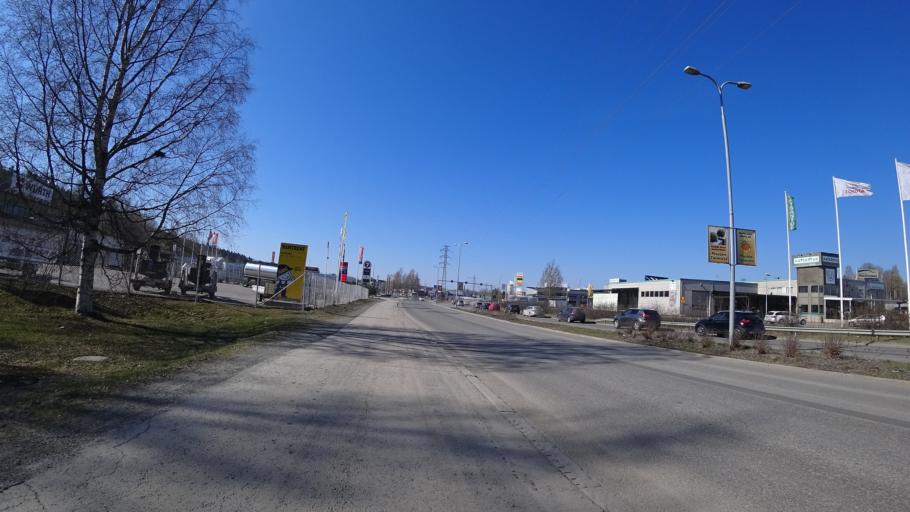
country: FI
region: Pirkanmaa
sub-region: Tampere
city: Pirkkala
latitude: 61.5129
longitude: 23.6765
